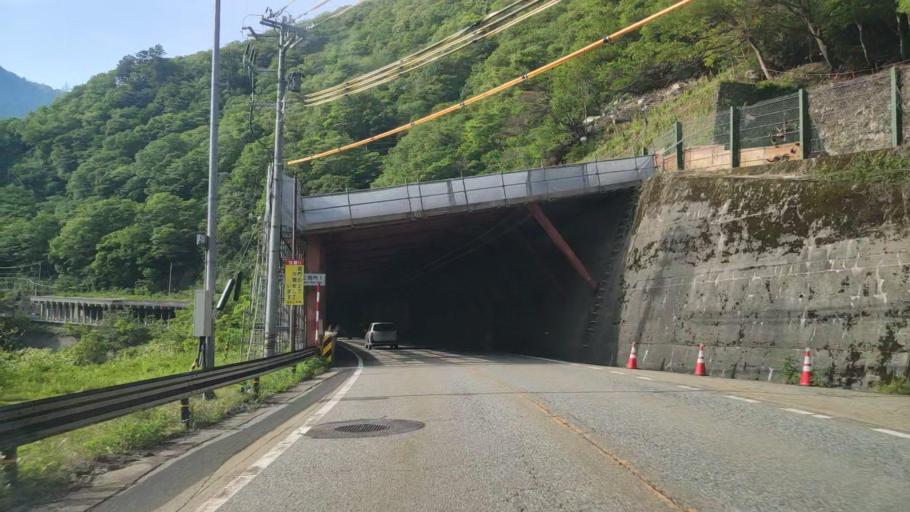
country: JP
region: Toyama
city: Yatsuomachi-higashikumisaka
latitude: 36.3806
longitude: 137.2801
